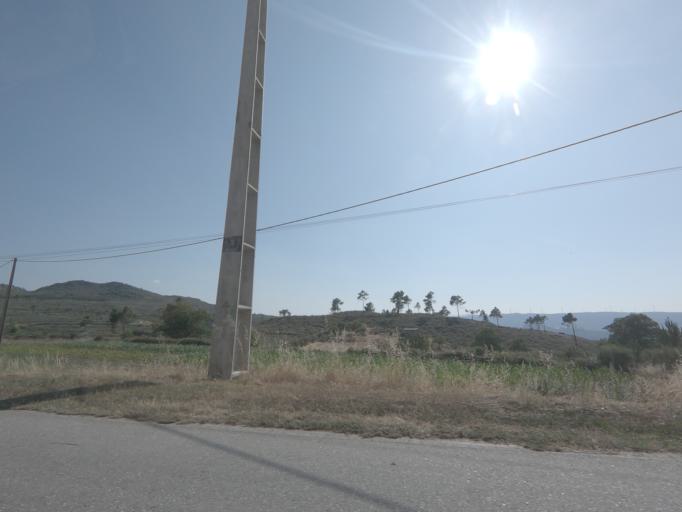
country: PT
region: Viseu
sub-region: Moimenta da Beira
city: Moimenta da Beira
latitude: 41.0408
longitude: -7.5706
